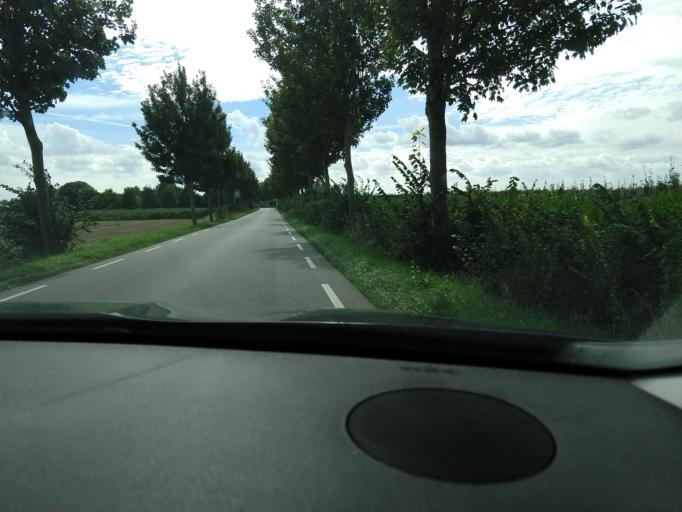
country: NL
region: Zeeland
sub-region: Gemeente Goes
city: Goes
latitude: 51.4250
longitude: 3.8810
